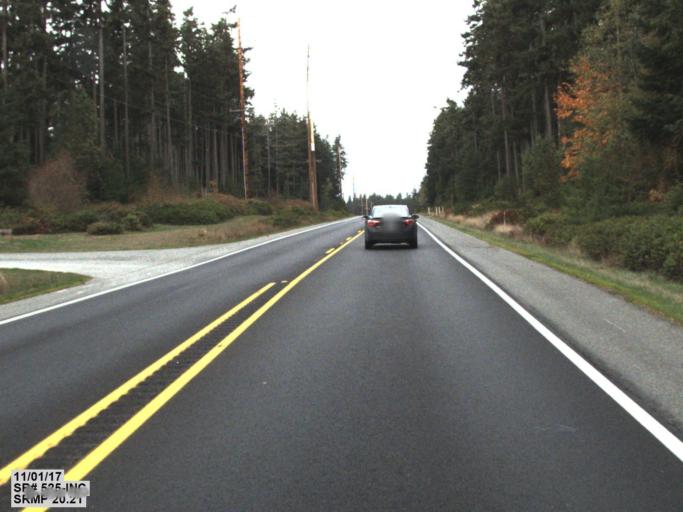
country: US
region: Washington
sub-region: Island County
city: Freeland
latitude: 48.0294
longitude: -122.5616
